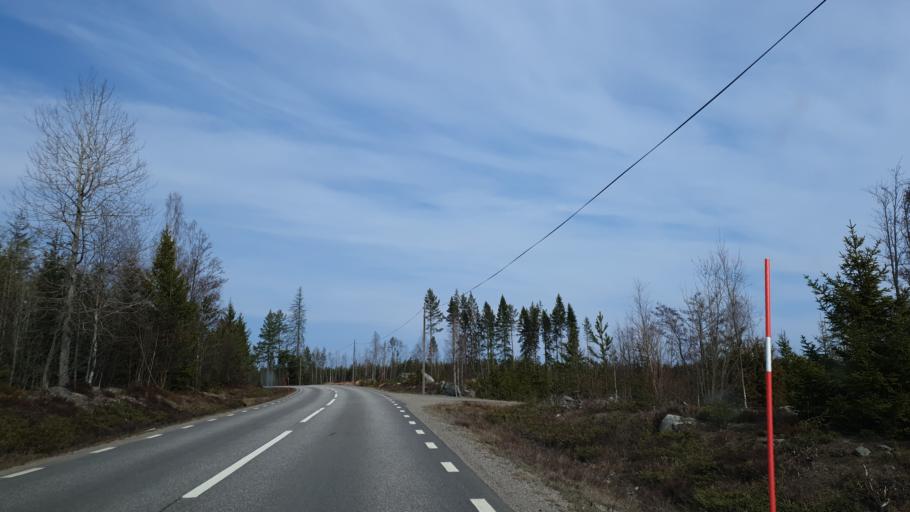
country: SE
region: Gaevleborg
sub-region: Gavle Kommun
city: Norrsundet
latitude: 61.0151
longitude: 17.1418
